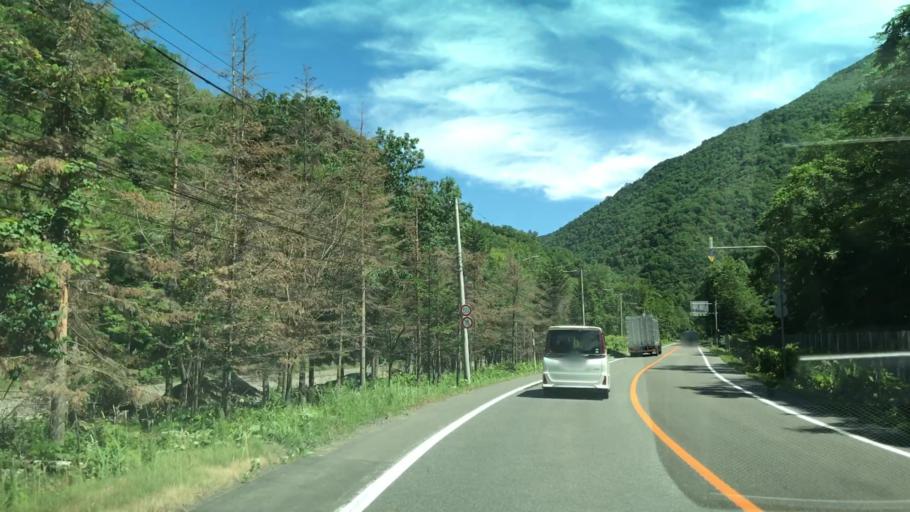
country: JP
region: Hokkaido
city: Shimo-furano
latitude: 42.9182
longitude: 142.5866
